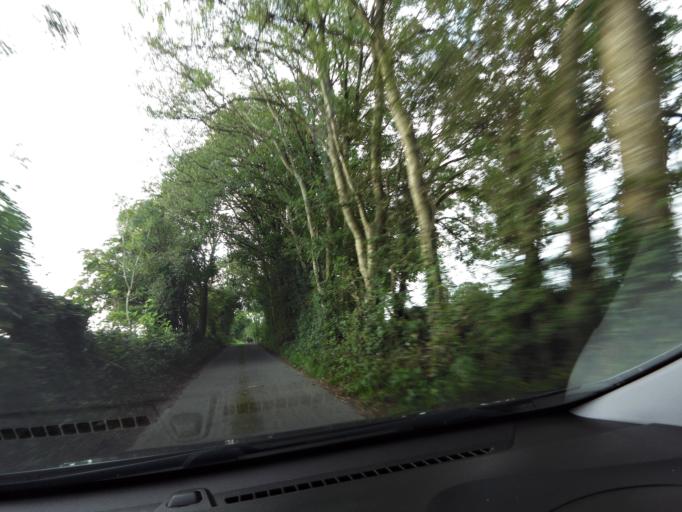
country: IE
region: Connaught
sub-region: County Galway
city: Ballinasloe
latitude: 53.3089
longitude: -8.1007
